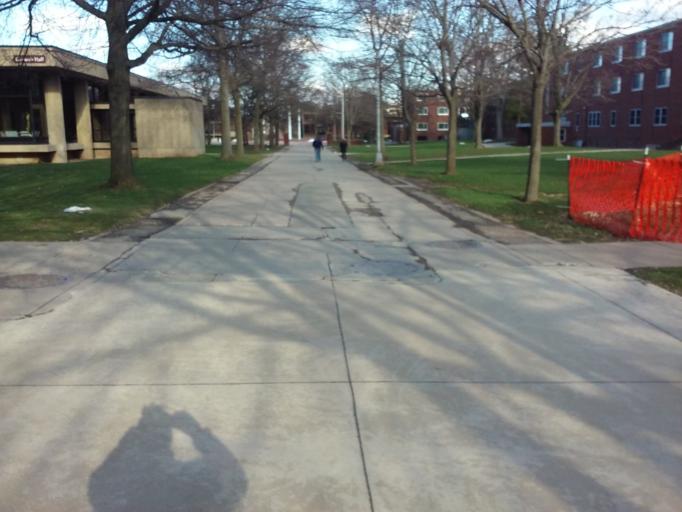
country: US
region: New York
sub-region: Monroe County
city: Brockport
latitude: 43.2123
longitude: -77.9500
